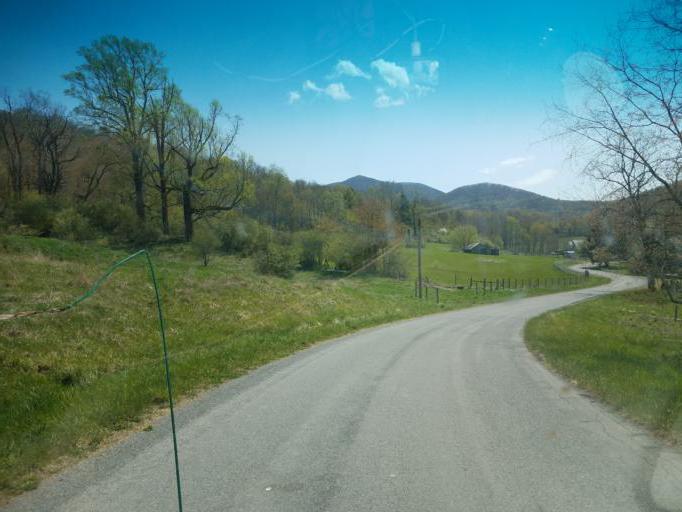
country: US
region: Virginia
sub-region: Smyth County
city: Marion
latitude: 36.7593
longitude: -81.4680
